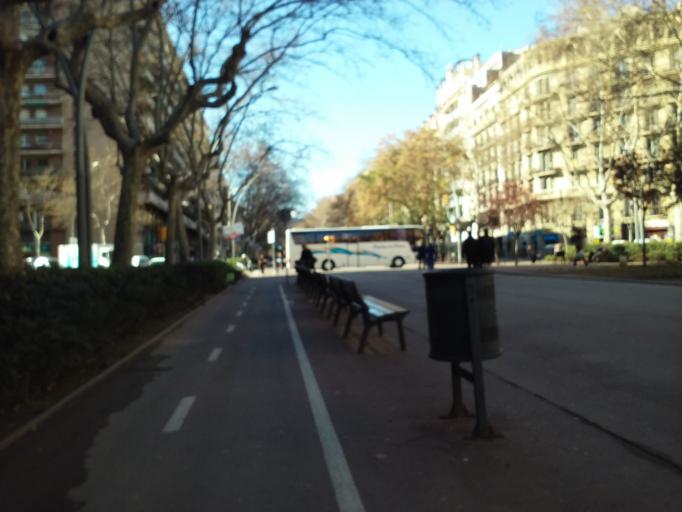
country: ES
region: Catalonia
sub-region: Provincia de Barcelona
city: Gracia
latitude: 41.4007
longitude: 2.1682
